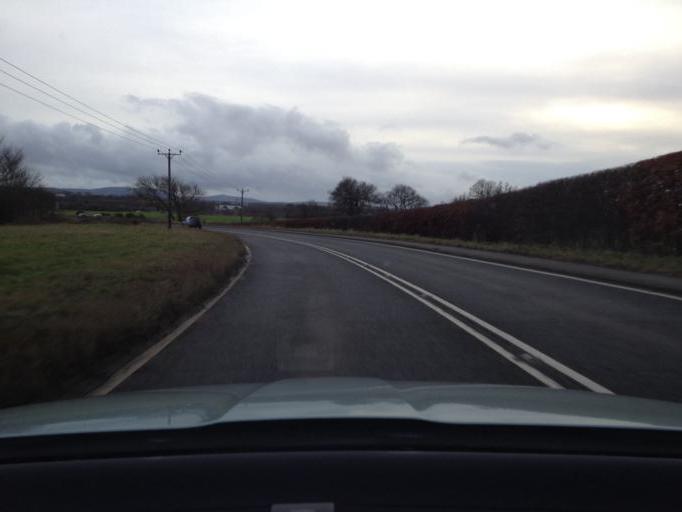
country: GB
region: Scotland
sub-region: Edinburgh
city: Kirkliston
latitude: 55.9451
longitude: -3.4139
